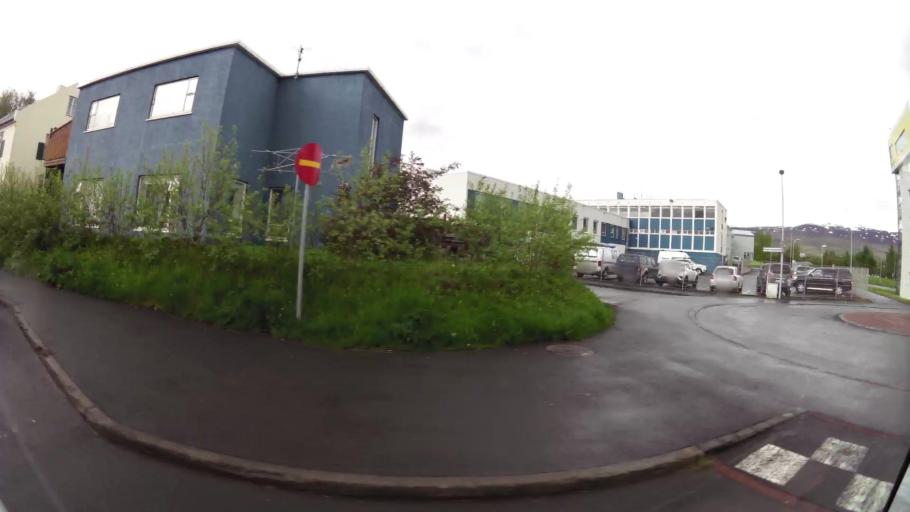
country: IS
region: Northeast
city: Akureyri
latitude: 65.6861
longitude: -18.0987
